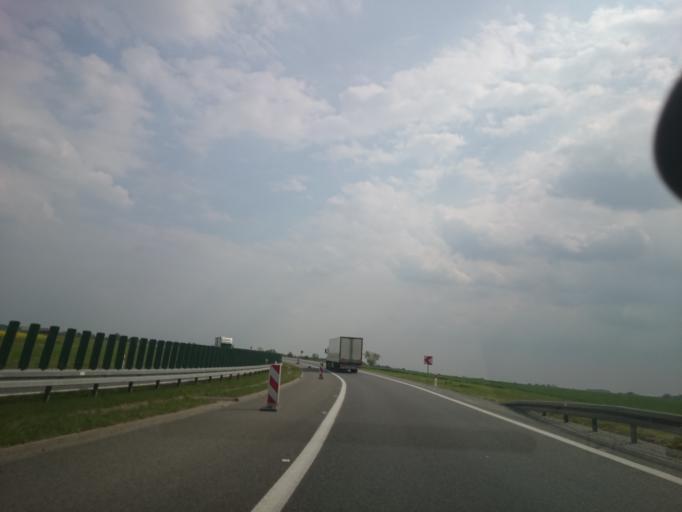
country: PL
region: Lower Silesian Voivodeship
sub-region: Powiat wroclawski
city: Tyniec Maly
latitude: 51.0048
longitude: 16.9385
